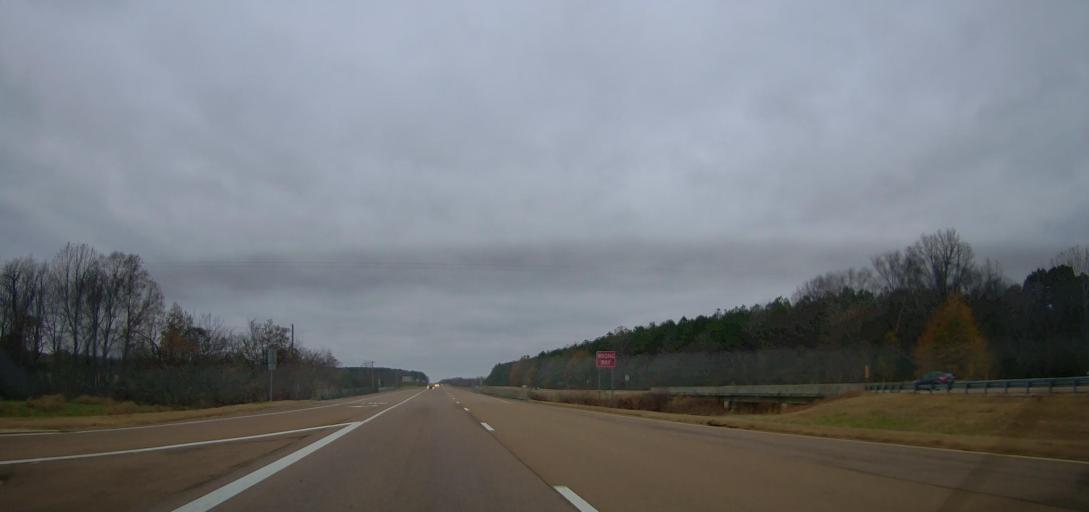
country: US
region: Mississippi
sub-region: Benton County
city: Ashland
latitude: 34.9461
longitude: -89.2114
